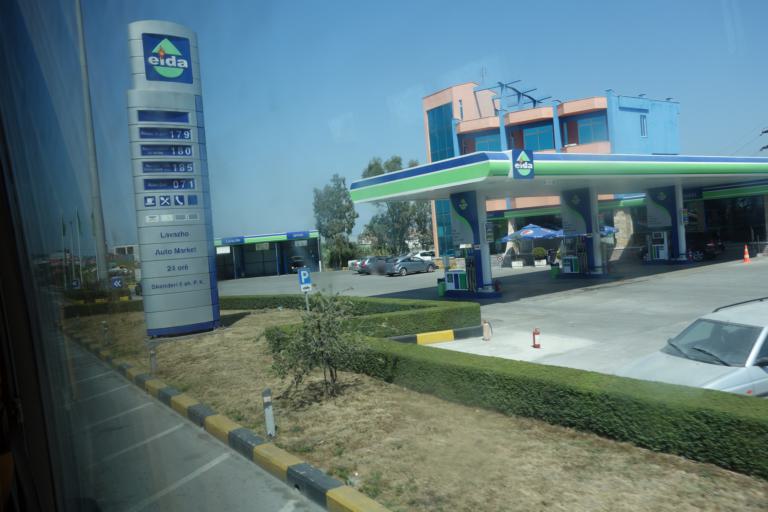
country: AL
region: Durres
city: Durres
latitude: 41.3259
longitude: 19.4715
